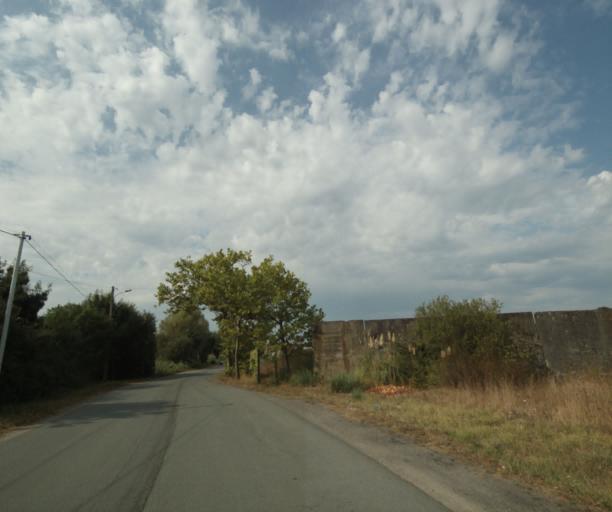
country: FR
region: Poitou-Charentes
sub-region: Departement de la Charente-Maritime
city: Tonnay-Charente
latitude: 45.9425
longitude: -0.9007
